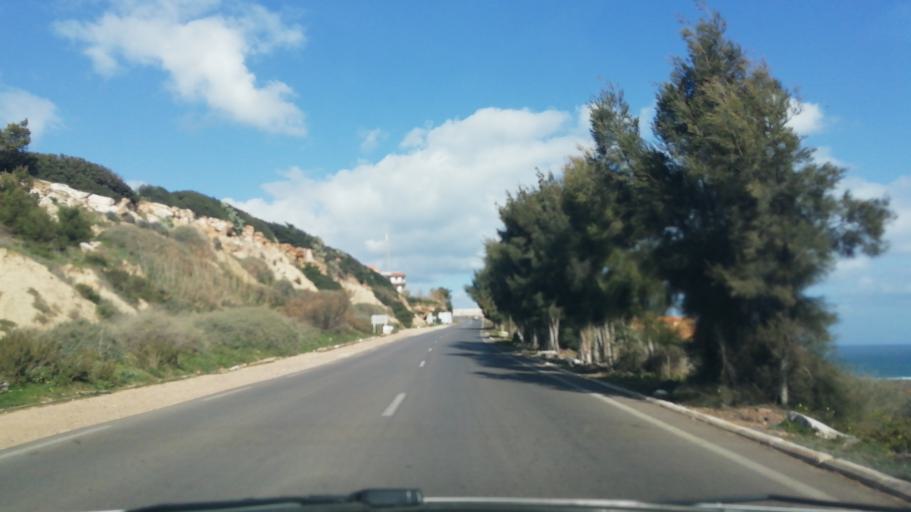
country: DZ
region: Relizane
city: Mazouna
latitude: 36.3211
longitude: 0.6794
